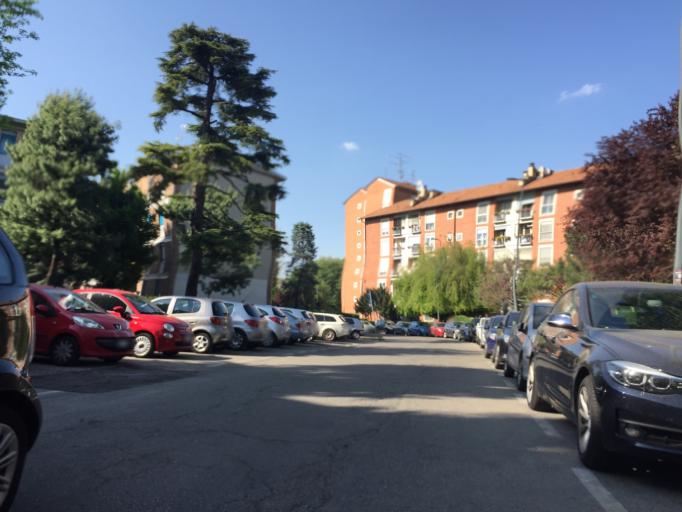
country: IT
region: Lombardy
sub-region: Citta metropolitana di Milano
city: Linate
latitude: 45.4594
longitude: 9.2468
